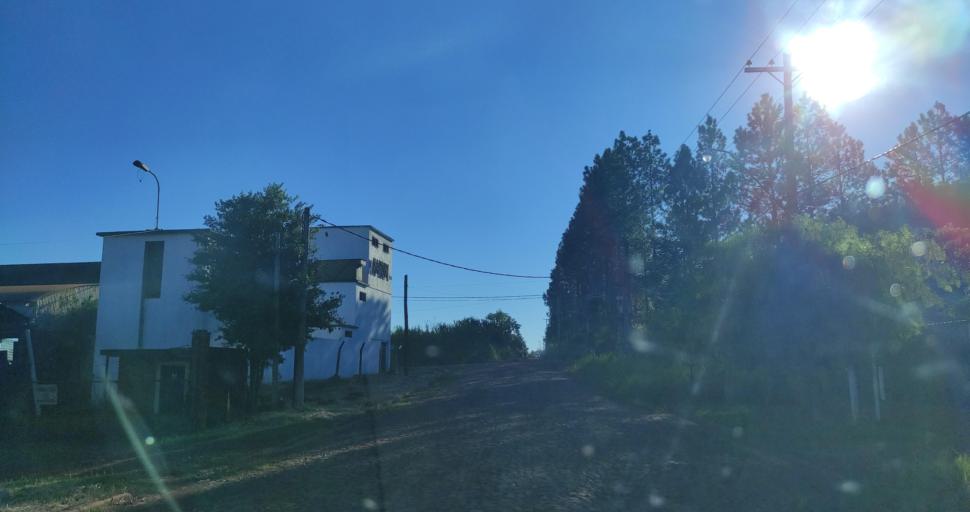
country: AR
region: Misiones
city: Puerto Rico
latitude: -26.8253
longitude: -55.0105
